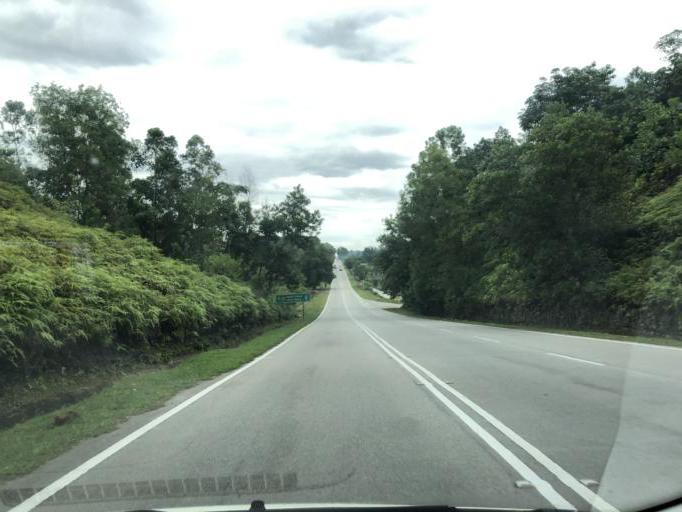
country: MY
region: Putrajaya
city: Putrajaya
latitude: 2.9249
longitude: 101.7472
